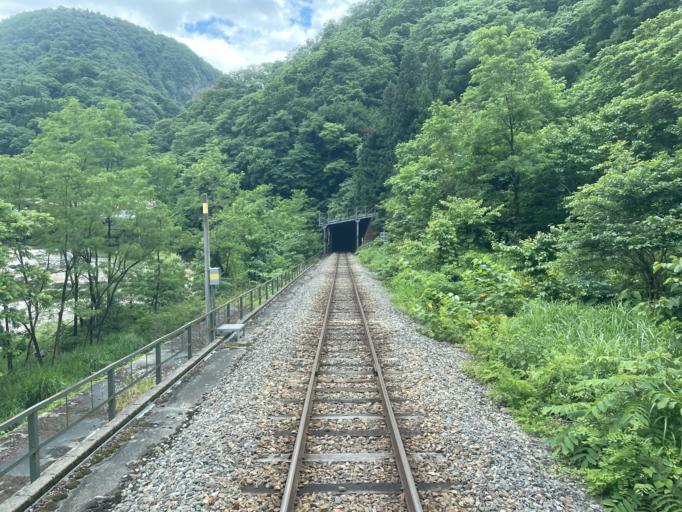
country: JP
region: Nagano
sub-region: Kitaazumi Gun
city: Hakuba
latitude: 36.8144
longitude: 137.9065
